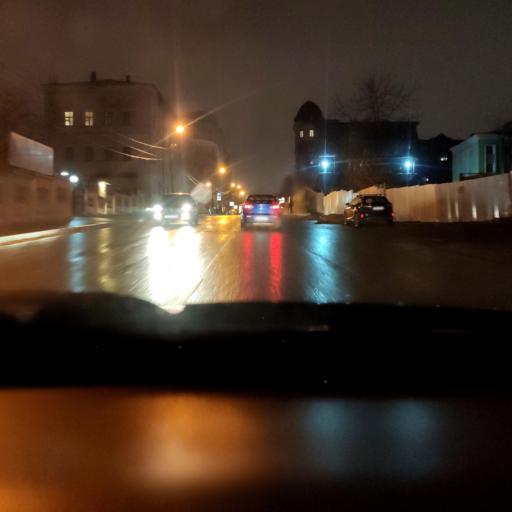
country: RU
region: Perm
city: Perm
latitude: 58.0187
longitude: 56.2532
